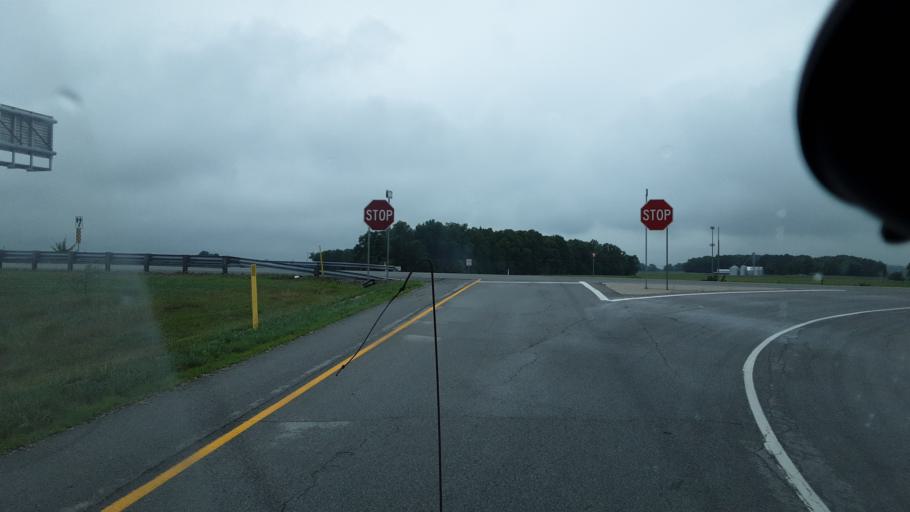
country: US
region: Indiana
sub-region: Wells County
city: Ossian
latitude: 40.9681
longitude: -85.1233
